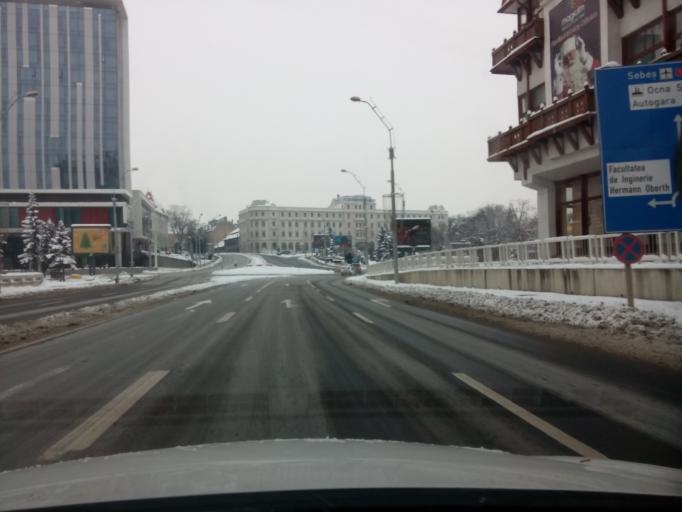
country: RO
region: Sibiu
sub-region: Municipiul Sibiu
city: Sibiu
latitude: 45.7902
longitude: 24.1493
